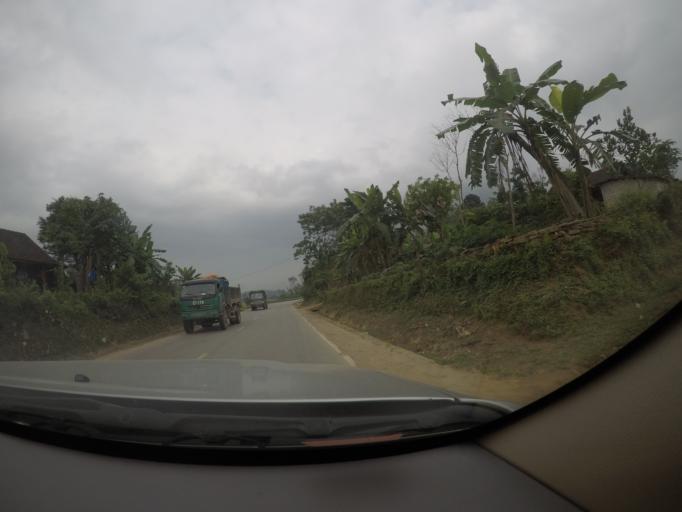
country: VN
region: Quang Binh
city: Ba Don
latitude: 17.6167
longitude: 106.3581
